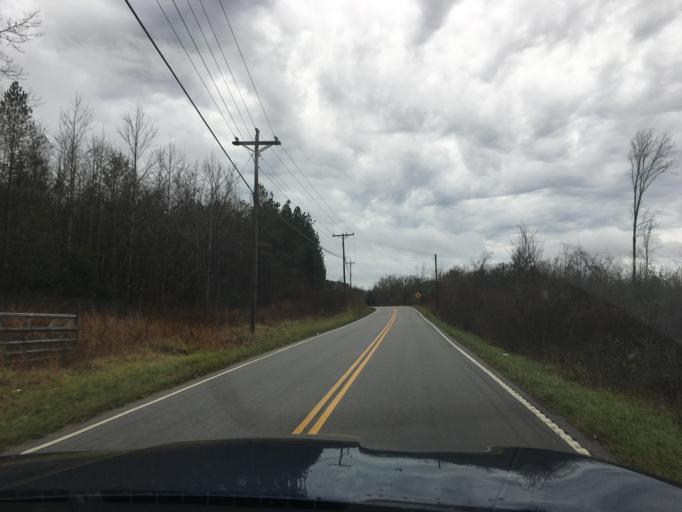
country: US
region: Tennessee
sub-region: Monroe County
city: Madisonville
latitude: 35.3690
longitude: -84.3193
